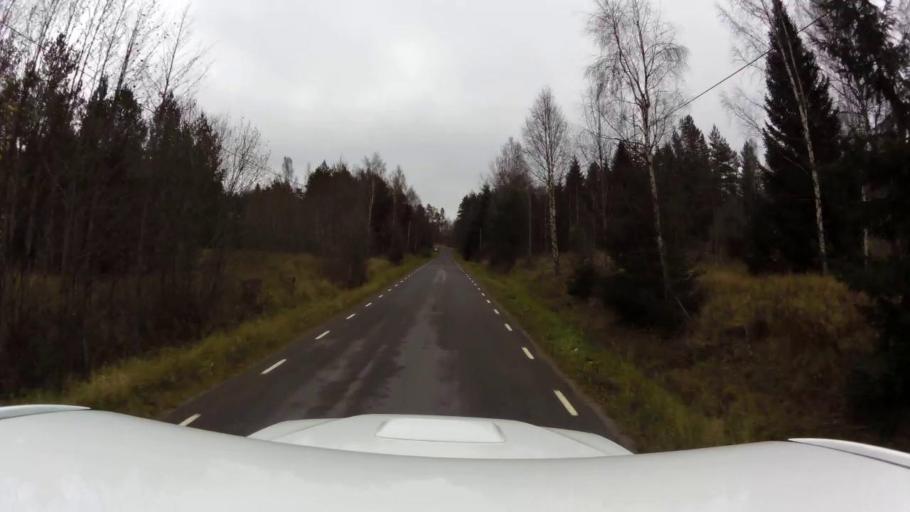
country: SE
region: OEstergoetland
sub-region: Kinda Kommun
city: Kisa
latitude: 58.1259
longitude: 15.4452
